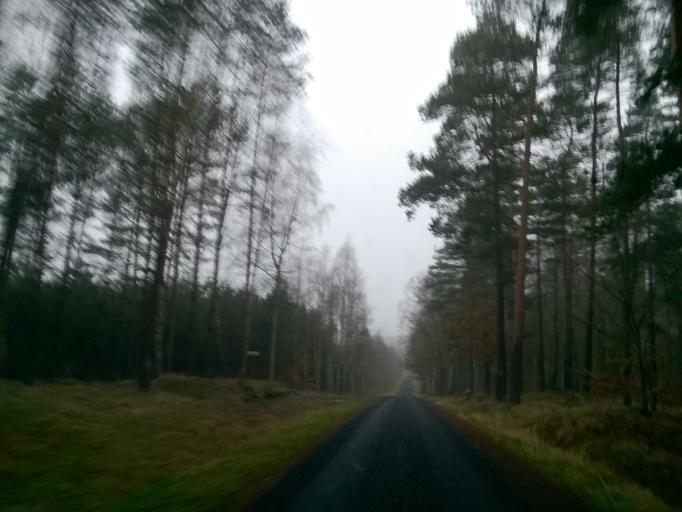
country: PL
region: Kujawsko-Pomorskie
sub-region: Powiat nakielski
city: Kcynia
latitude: 53.0517
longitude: 17.4620
